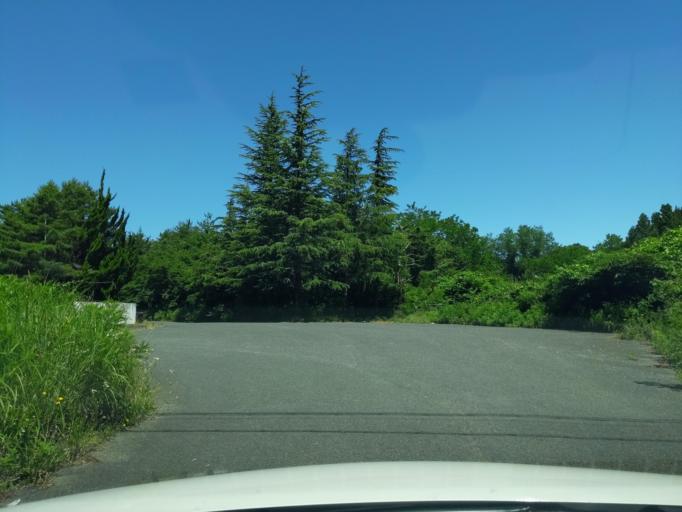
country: JP
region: Fukushima
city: Koriyama
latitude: 37.3856
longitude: 140.2573
